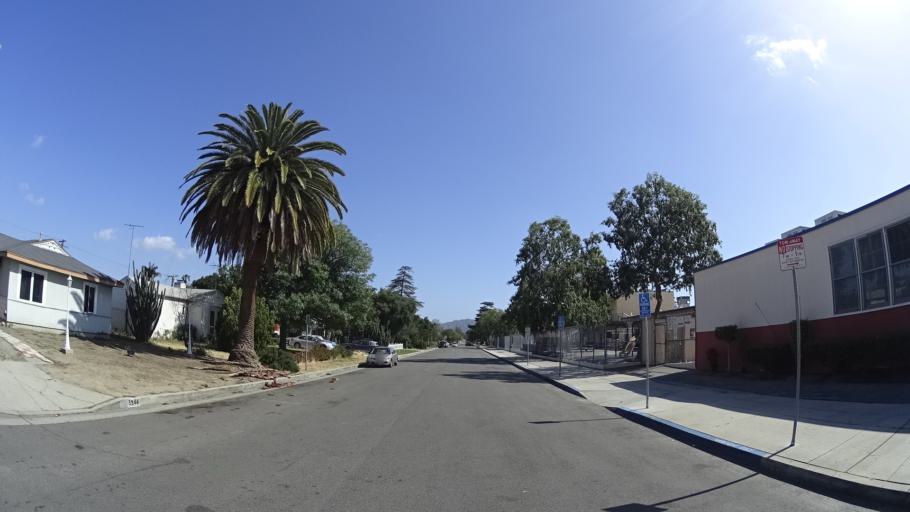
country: US
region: California
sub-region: Los Angeles County
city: North Hollywood
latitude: 34.1789
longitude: -118.3682
